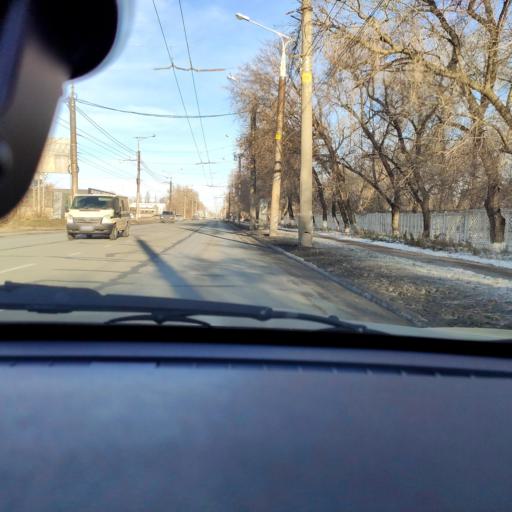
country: RU
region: Samara
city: Tol'yatti
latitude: 53.5248
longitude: 49.4349
